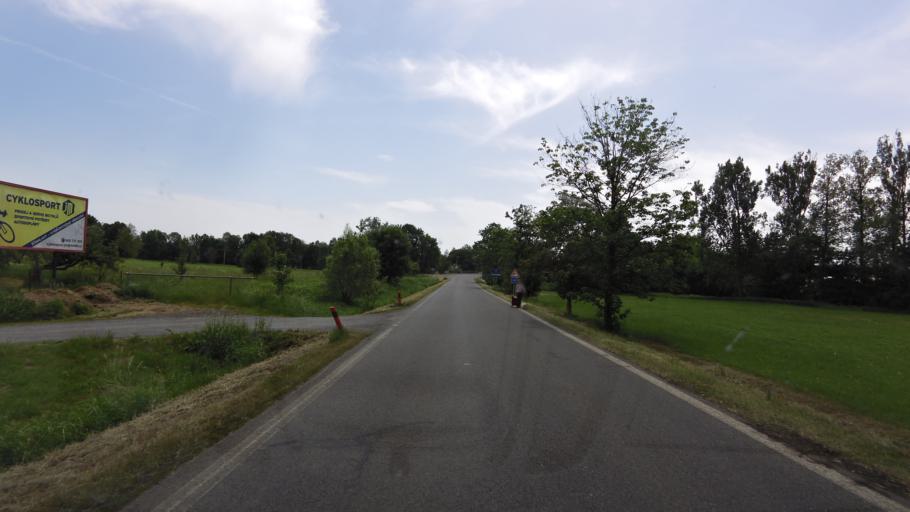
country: CZ
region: Plzensky
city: St'ahlavy
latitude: 49.6779
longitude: 13.5093
